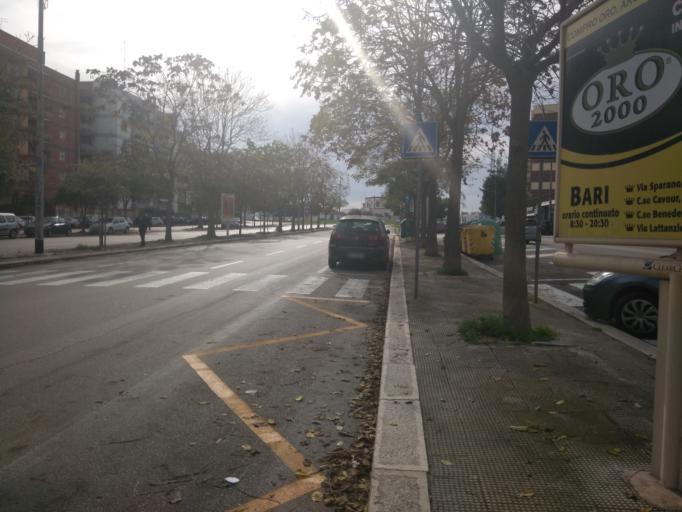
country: IT
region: Apulia
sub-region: Provincia di Bari
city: Bari
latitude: 41.1117
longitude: 16.8915
